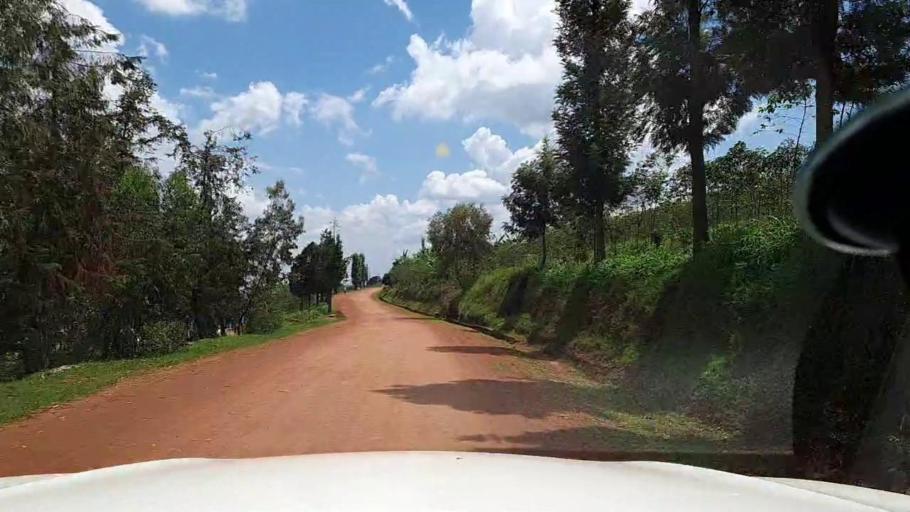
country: RW
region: Kigali
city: Kigali
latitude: -1.7914
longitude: 29.8442
